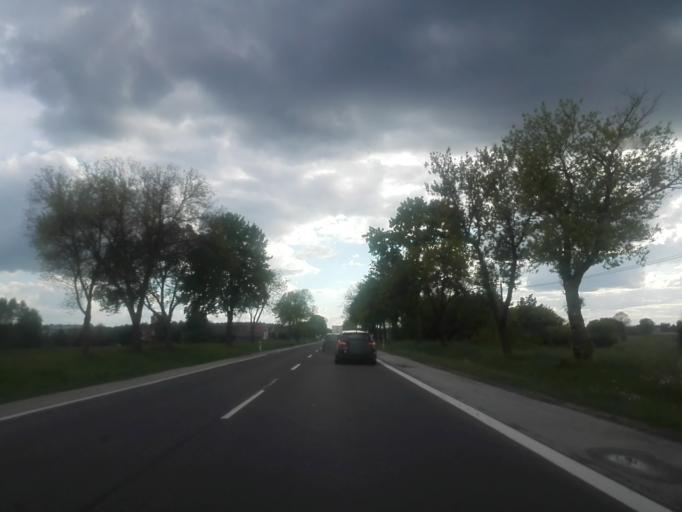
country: PL
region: Masovian Voivodeship
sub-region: Powiat ostrowski
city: Brok
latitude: 52.7596
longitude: 21.8011
